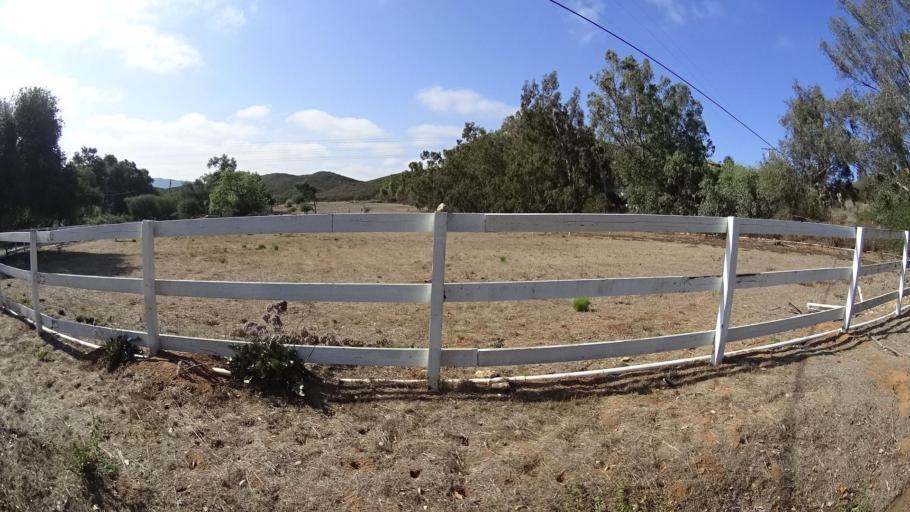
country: US
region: California
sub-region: San Diego County
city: Lake San Marcos
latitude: 33.0976
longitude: -117.1726
